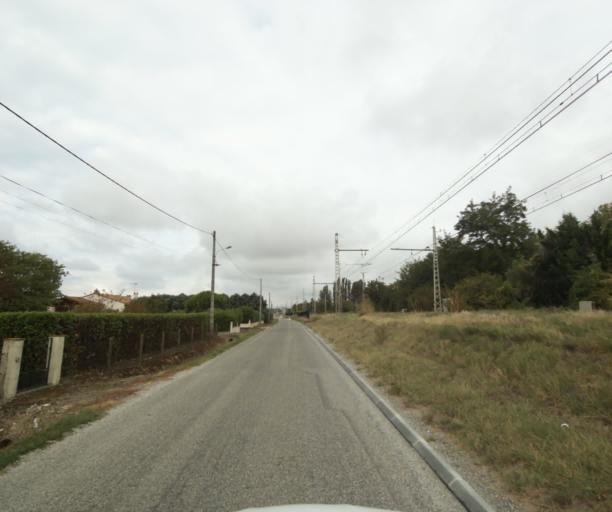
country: FR
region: Midi-Pyrenees
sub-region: Departement de la Haute-Garonne
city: Villefranche-de-Lauragais
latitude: 43.3925
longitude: 1.7226
